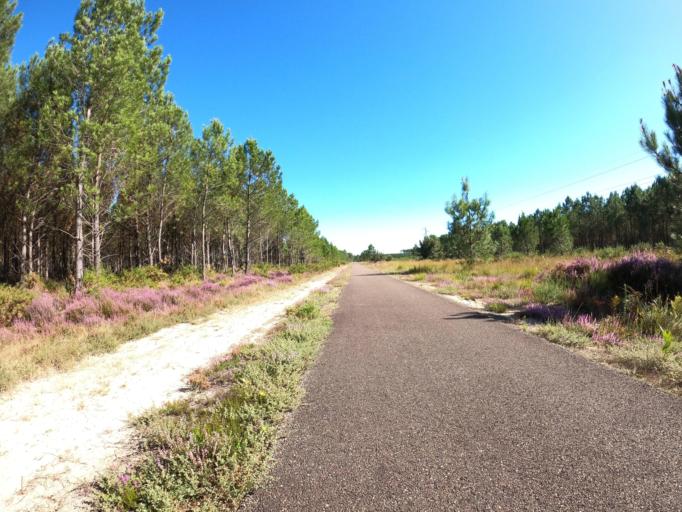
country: FR
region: Aquitaine
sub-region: Departement des Landes
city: Ychoux
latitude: 44.3388
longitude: -0.9600
